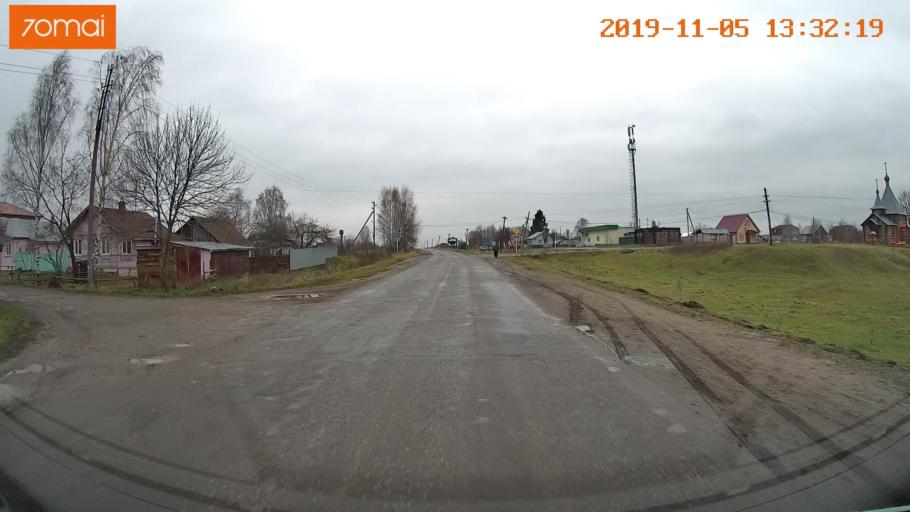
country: RU
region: Ivanovo
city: Shuya
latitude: 56.8823
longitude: 41.3981
